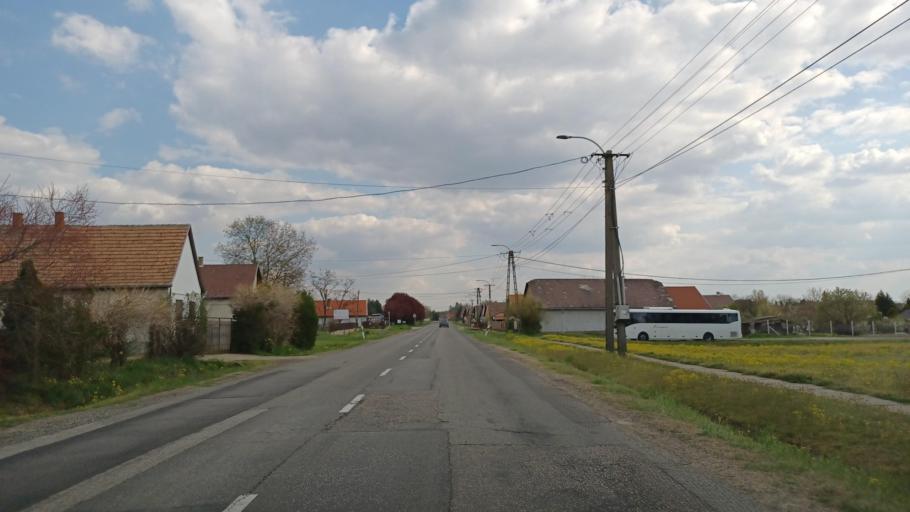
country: HU
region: Fejer
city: Cece
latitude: 46.7240
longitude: 18.6611
